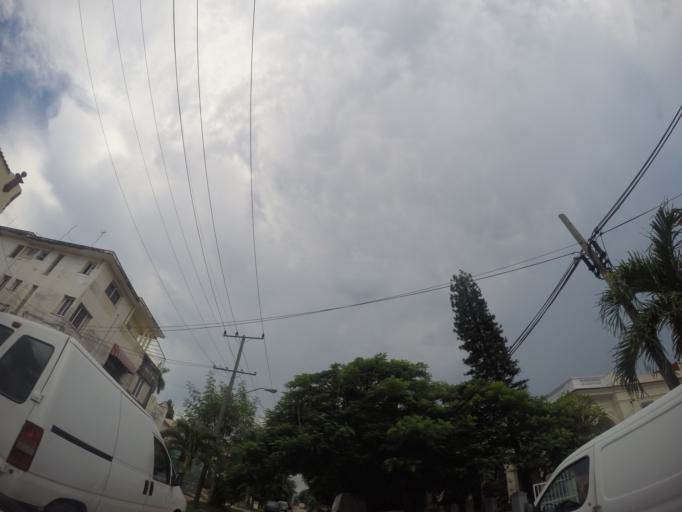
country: CU
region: La Habana
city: Havana
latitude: 23.1209
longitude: -82.4205
